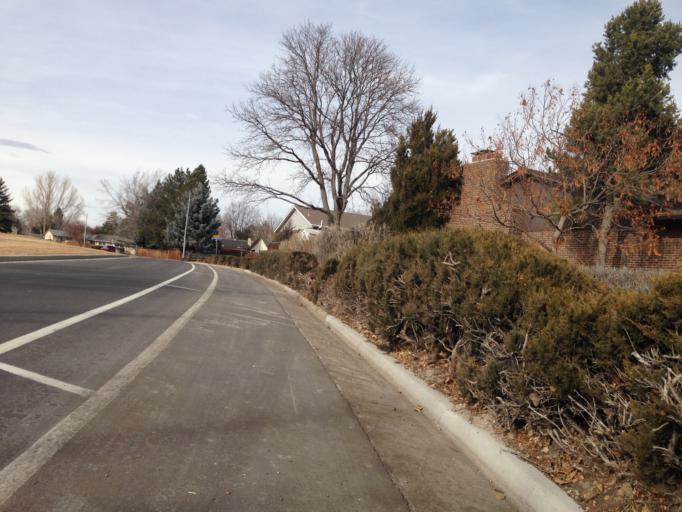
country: US
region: Colorado
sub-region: Adams County
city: Westminster
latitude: 39.8459
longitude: -105.0771
